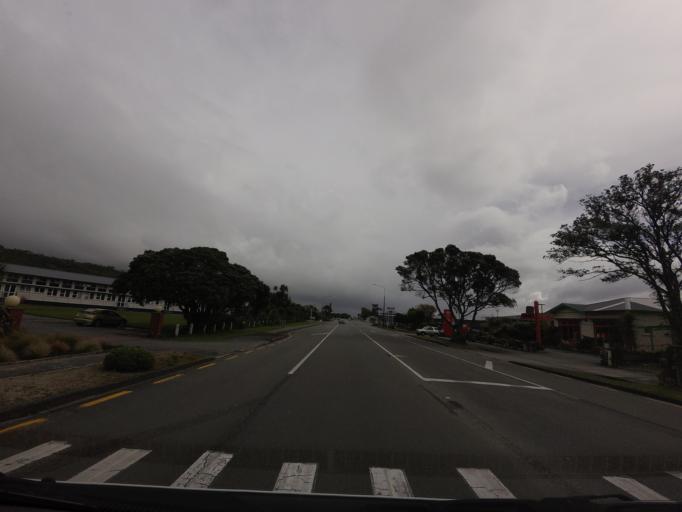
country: NZ
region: West Coast
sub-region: Grey District
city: Greymouth
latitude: -42.4622
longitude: 171.1969
